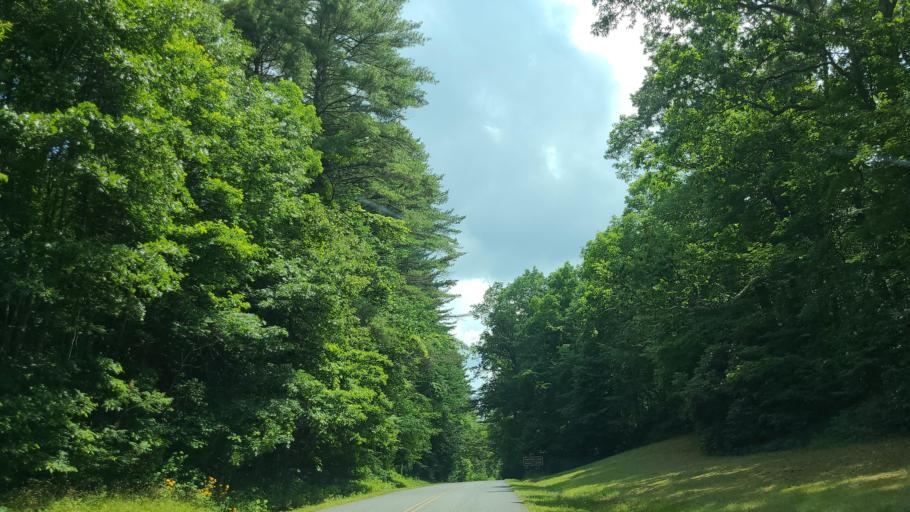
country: US
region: North Carolina
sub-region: Avery County
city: Newland
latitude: 35.9697
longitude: -81.9448
